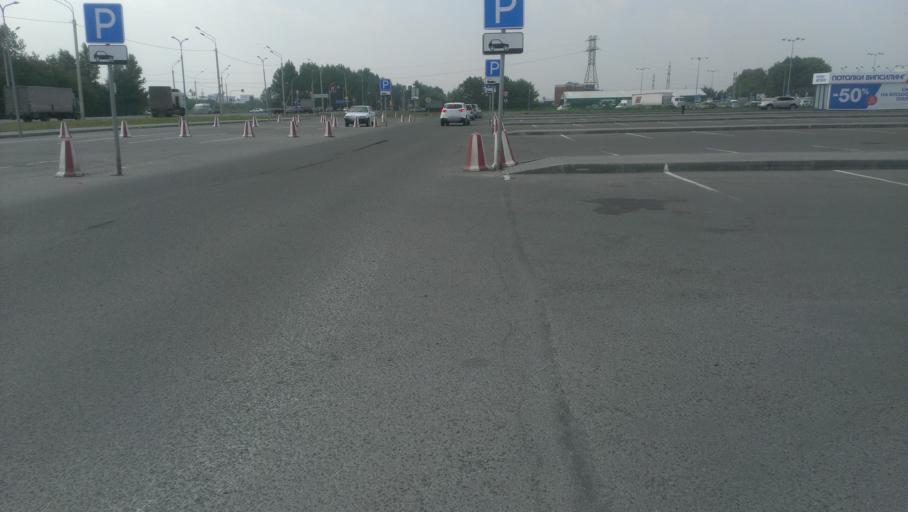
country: RU
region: Altai Krai
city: Novosilikatnyy
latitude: 53.3484
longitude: 83.6344
